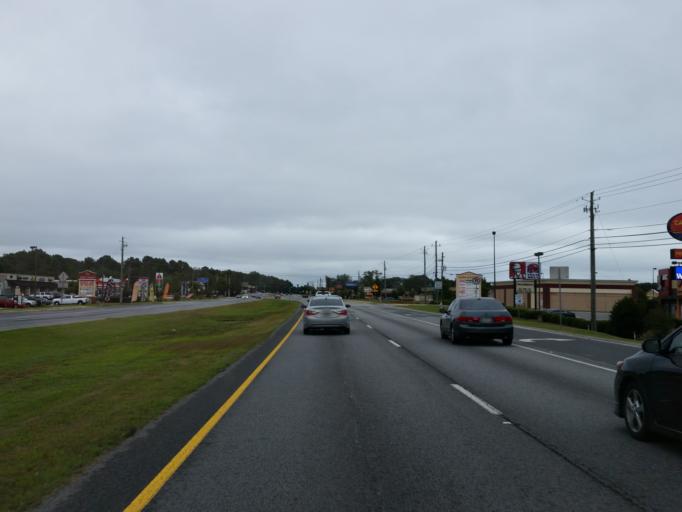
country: US
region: Georgia
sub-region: Clayton County
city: Lovejoy
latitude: 33.4470
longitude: -84.3245
